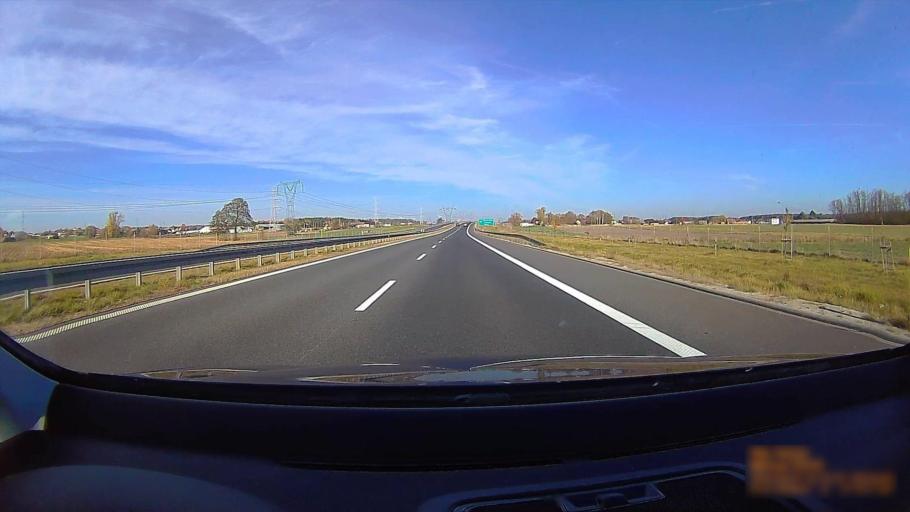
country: PL
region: Greater Poland Voivodeship
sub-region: Powiat ostrowski
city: Przygodzice
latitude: 51.6000
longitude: 17.8521
